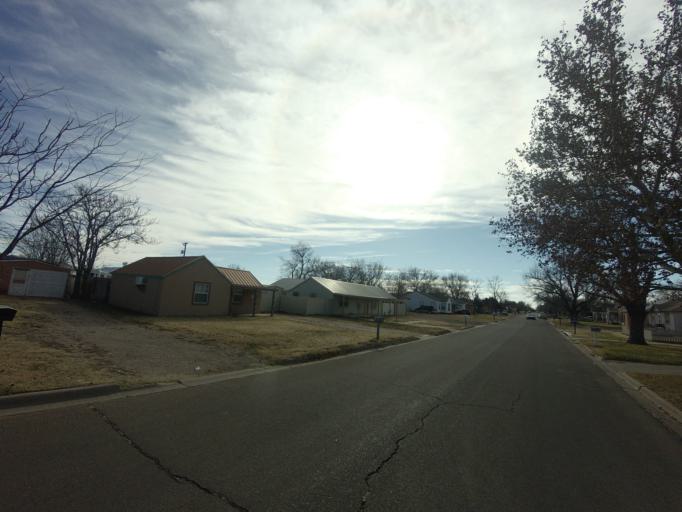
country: US
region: New Mexico
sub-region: Curry County
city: Clovis
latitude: 34.4144
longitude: -103.1978
